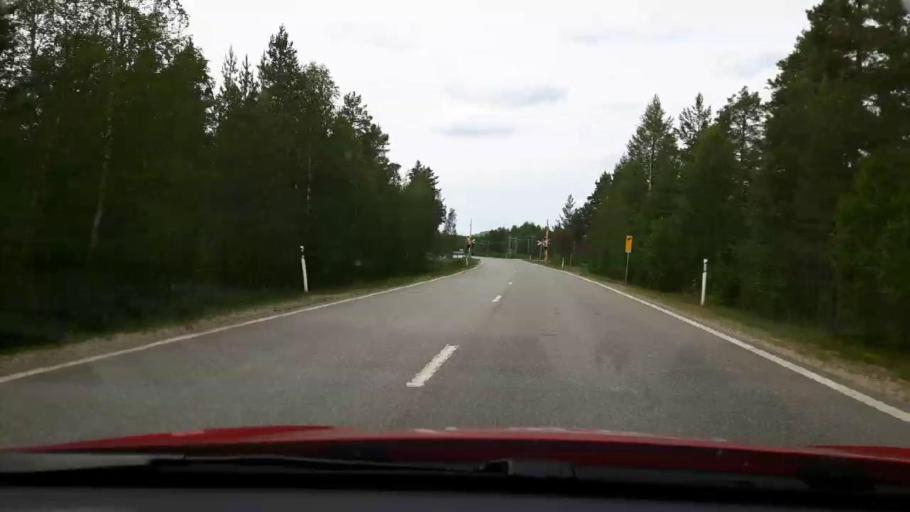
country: SE
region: Jaemtland
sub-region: Harjedalens Kommun
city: Sveg
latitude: 62.0431
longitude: 14.3561
